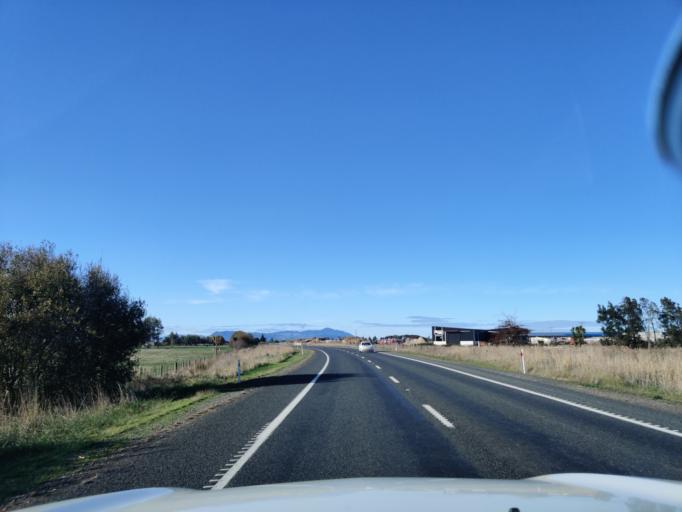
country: NZ
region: Waikato
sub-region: Hauraki District
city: Ngatea
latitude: -37.2936
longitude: 175.5518
